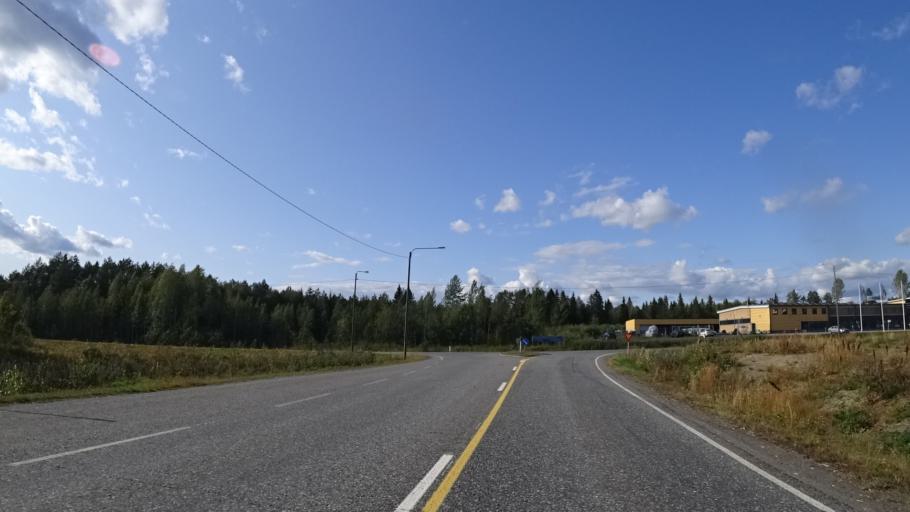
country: FI
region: North Karelia
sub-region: Keski-Karjala
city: Kitee
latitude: 62.0971
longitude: 30.1113
